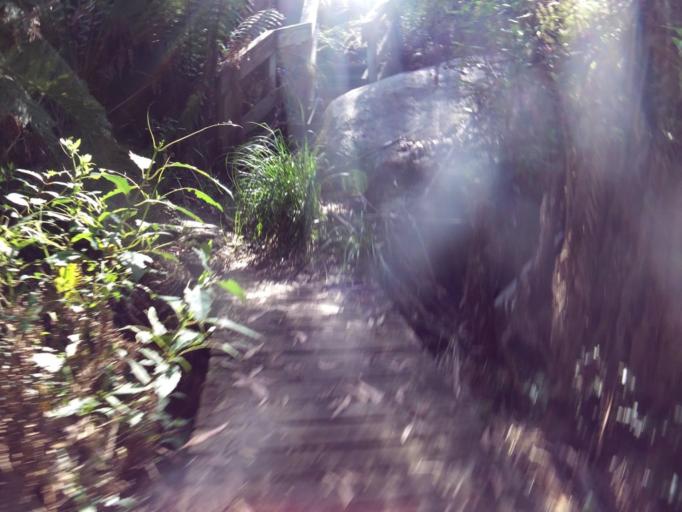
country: AU
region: Victoria
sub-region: Yarra Ranges
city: Millgrove
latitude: -37.4991
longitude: 145.8402
